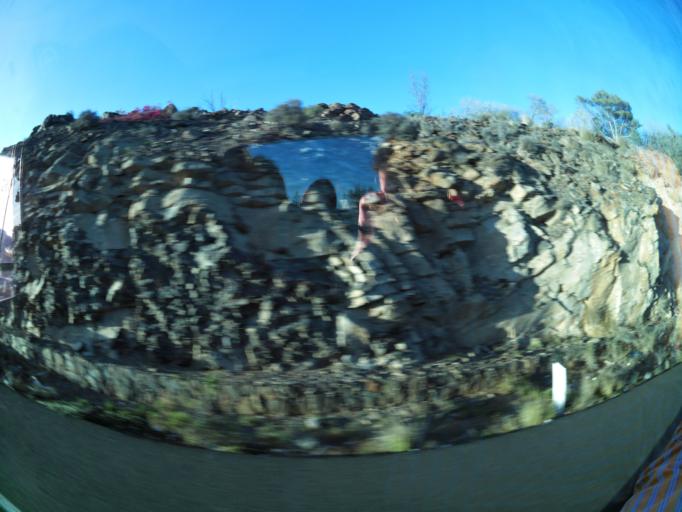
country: ES
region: Canary Islands
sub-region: Provincia de Las Palmas
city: Playa del Ingles
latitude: 27.7735
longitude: -15.5355
